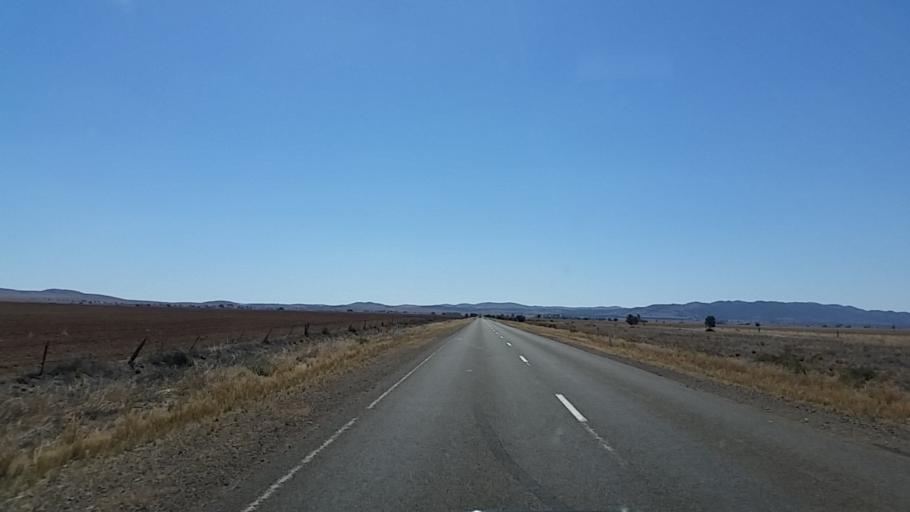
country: AU
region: South Australia
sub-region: Peterborough
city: Peterborough
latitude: -32.6636
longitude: 138.6063
